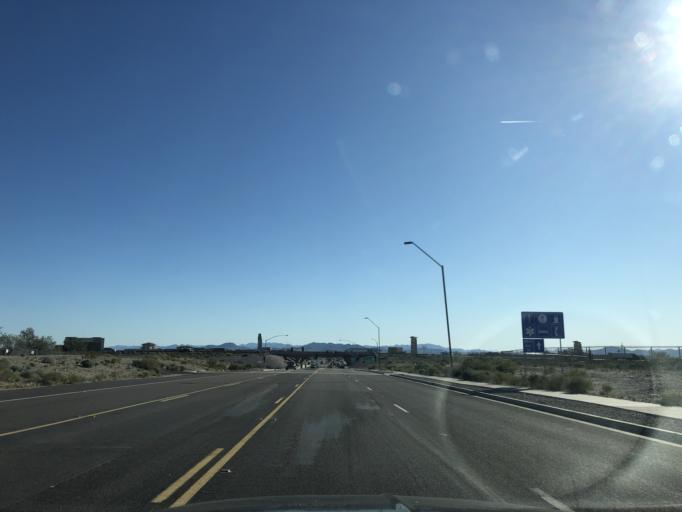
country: US
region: Arizona
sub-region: Maricopa County
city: Buckeye
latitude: 33.4475
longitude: -112.5565
